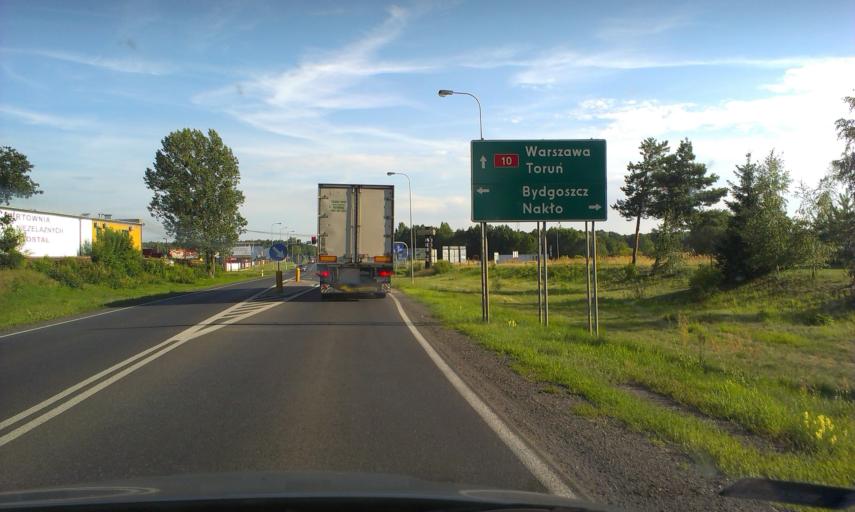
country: PL
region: Kujawsko-Pomorskie
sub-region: Powiat bydgoski
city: Biale Blota
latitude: 53.1285
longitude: 17.8807
